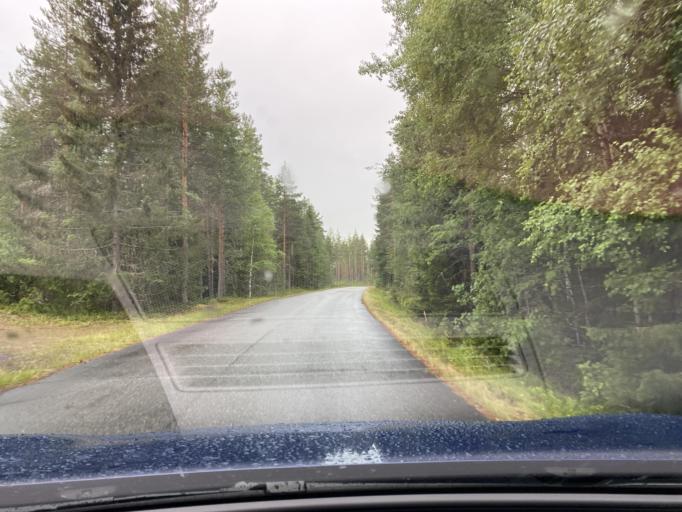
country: FI
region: Central Ostrobothnia
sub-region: Kaustinen
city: Halsua
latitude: 63.4155
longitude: 23.9772
